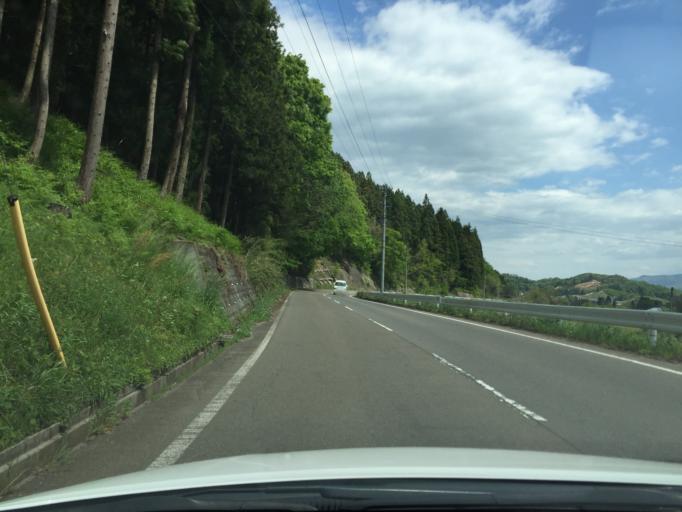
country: JP
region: Fukushima
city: Hobaramachi
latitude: 37.7598
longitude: 140.5714
